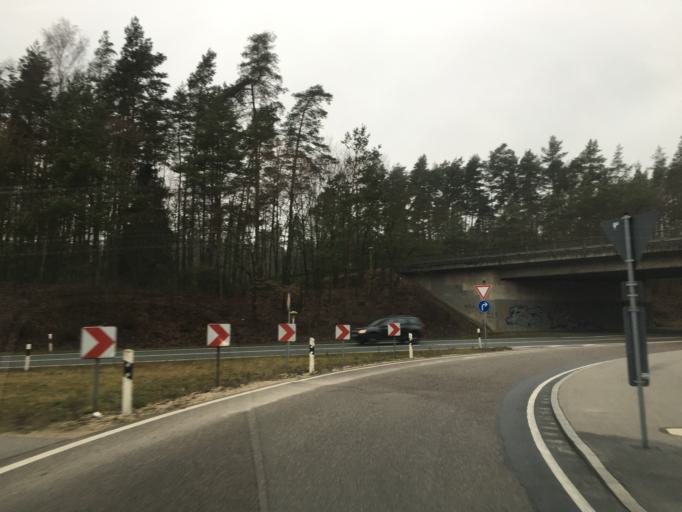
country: DE
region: Bavaria
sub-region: Regierungsbezirk Mittelfranken
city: Wendelstein
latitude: 49.3633
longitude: 11.1566
